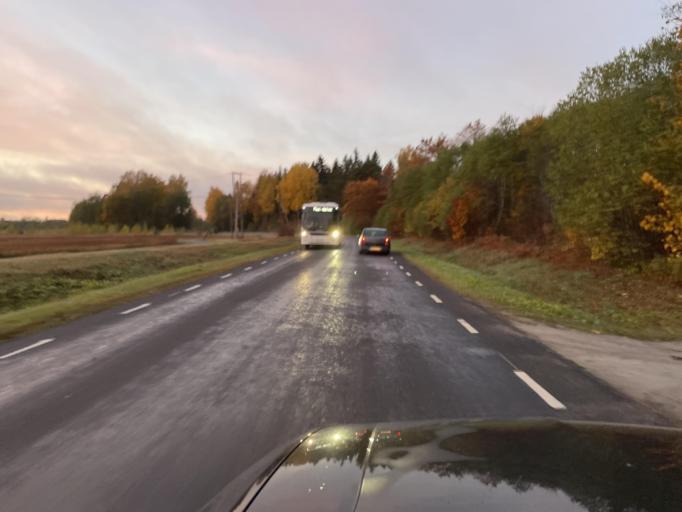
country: EE
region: Harju
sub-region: Nissi vald
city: Riisipere
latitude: 59.2385
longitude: 24.2440
